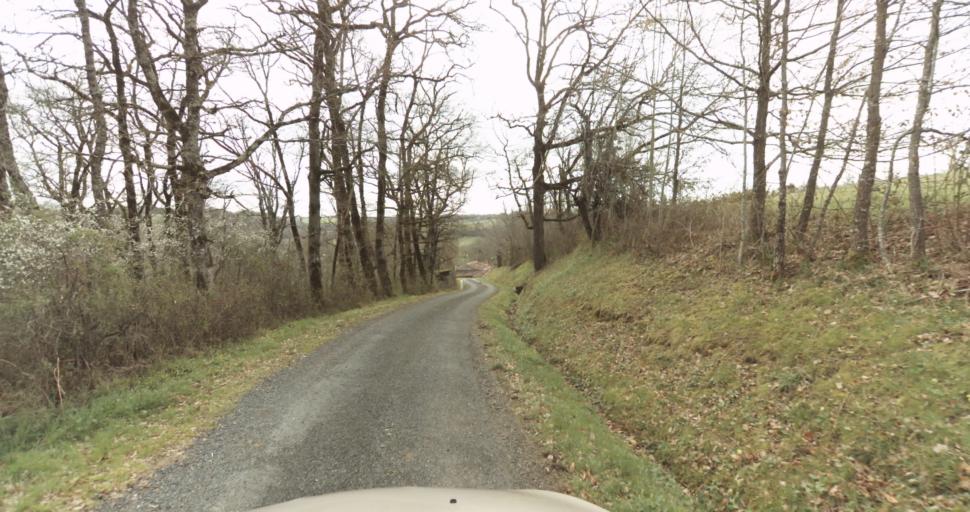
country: FR
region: Midi-Pyrenees
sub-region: Departement du Tarn
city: Frejairolles
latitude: 43.8518
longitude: 2.2249
